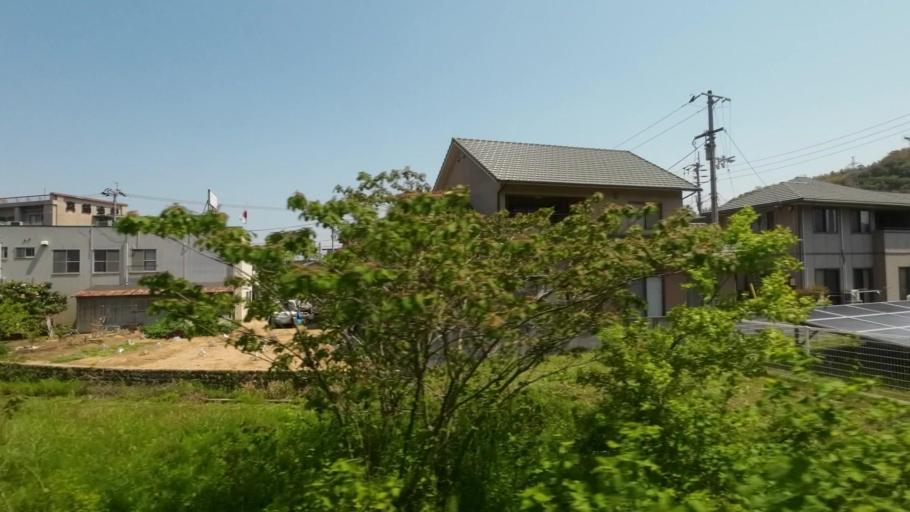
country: JP
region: Ehime
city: Hojo
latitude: 34.0955
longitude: 132.9728
